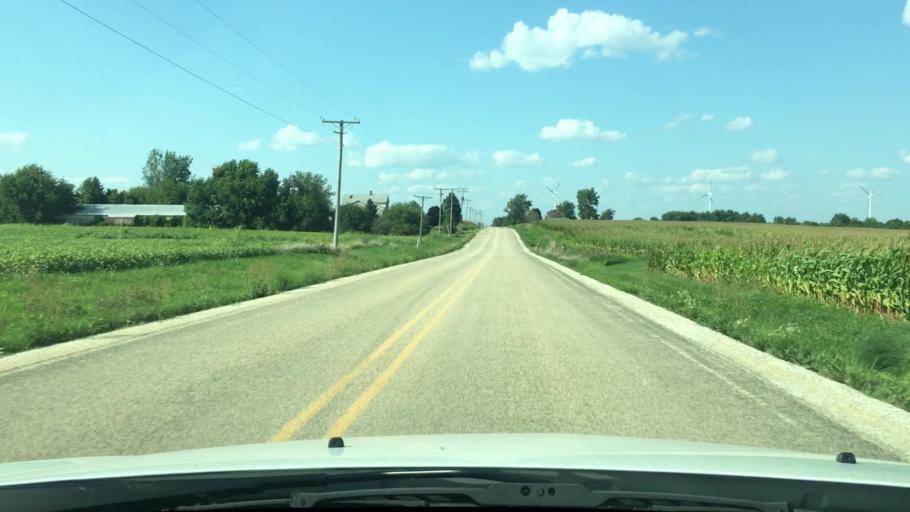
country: US
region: Illinois
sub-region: DeKalb County
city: Waterman
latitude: 41.8067
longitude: -88.7734
